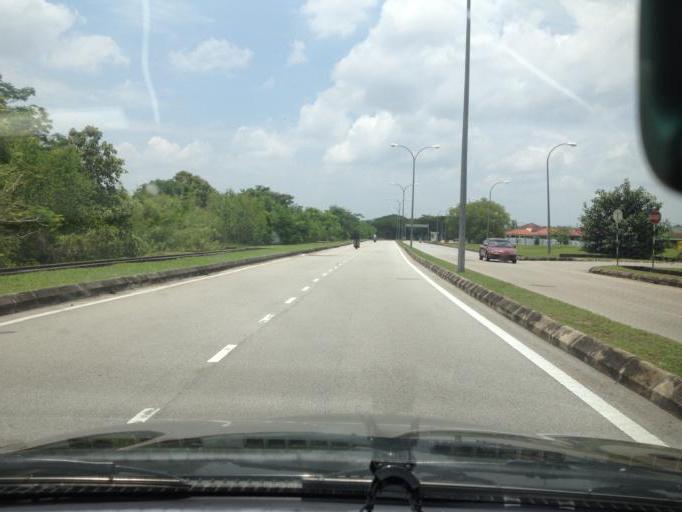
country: MY
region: Kedah
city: Sungai Petani
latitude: 5.6049
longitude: 100.5449
